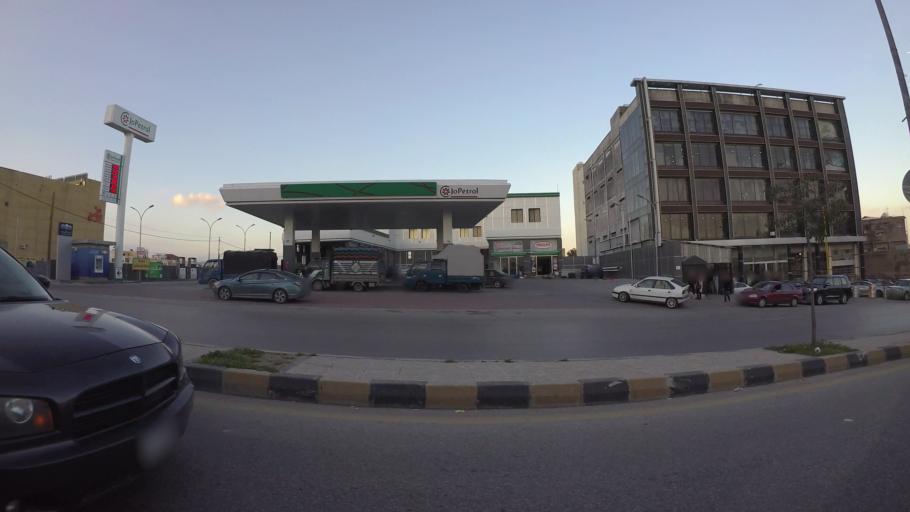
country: JO
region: Amman
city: Al Bunayyat ash Shamaliyah
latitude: 31.9174
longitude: 35.9024
